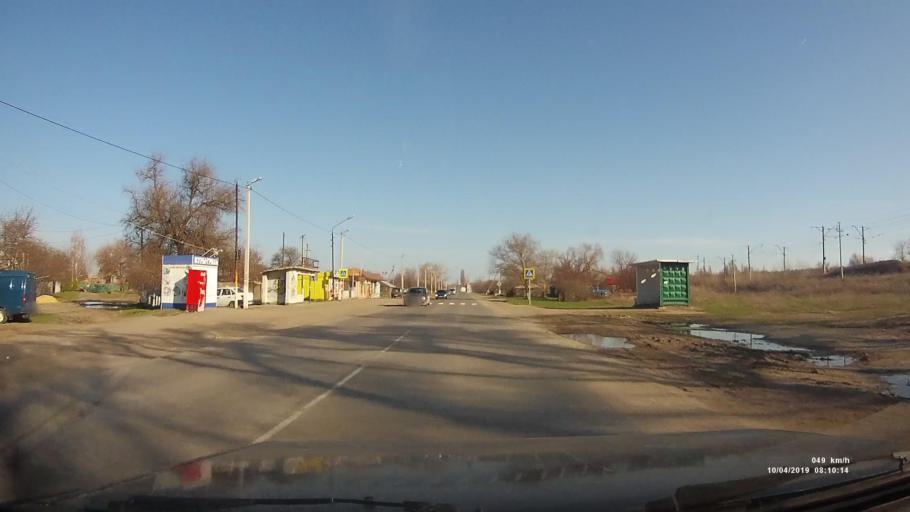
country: RU
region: Rostov
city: Staraya Stanitsa
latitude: 48.3507
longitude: 40.2703
